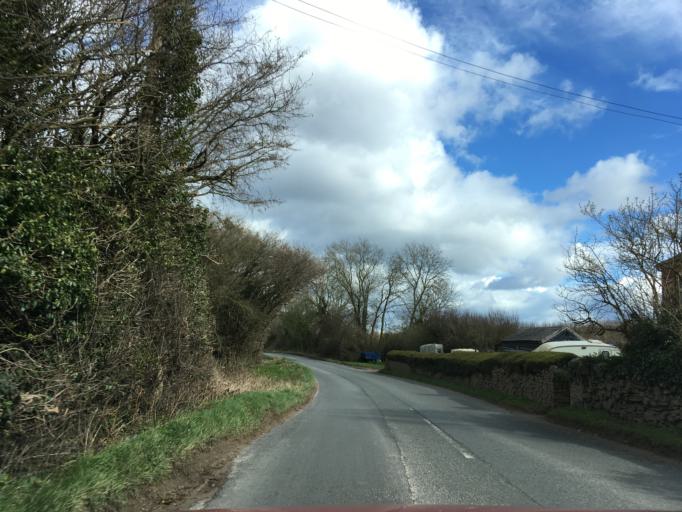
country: GB
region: England
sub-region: Gloucestershire
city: Coleford
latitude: 51.7596
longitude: -2.6254
